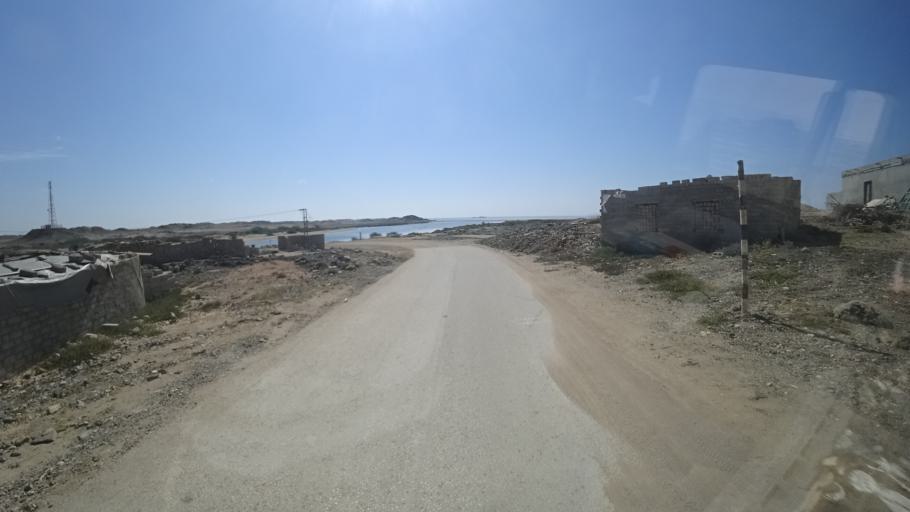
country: OM
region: Zufar
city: Salalah
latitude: 16.9631
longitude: 54.7457
